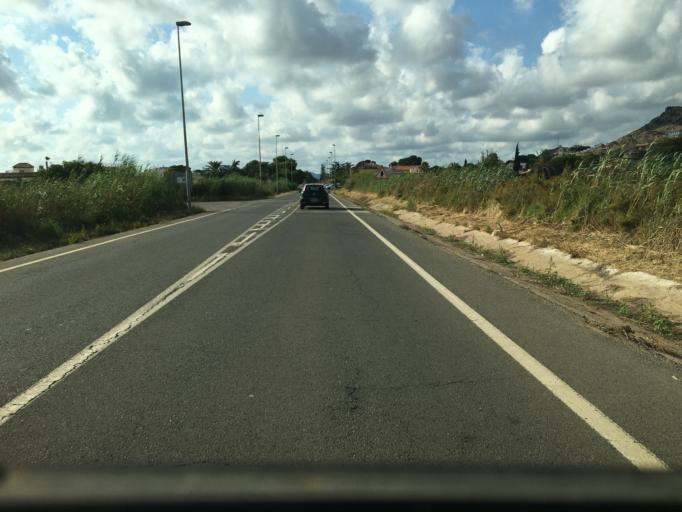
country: ES
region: Murcia
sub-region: Murcia
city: Los Alcazares
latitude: 37.6969
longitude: -0.8433
